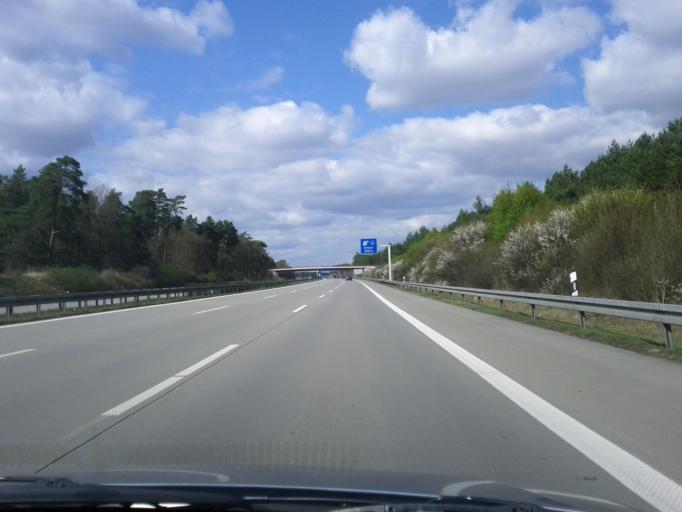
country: DE
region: Brandenburg
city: Grunheide
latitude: 52.4089
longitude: 13.7862
